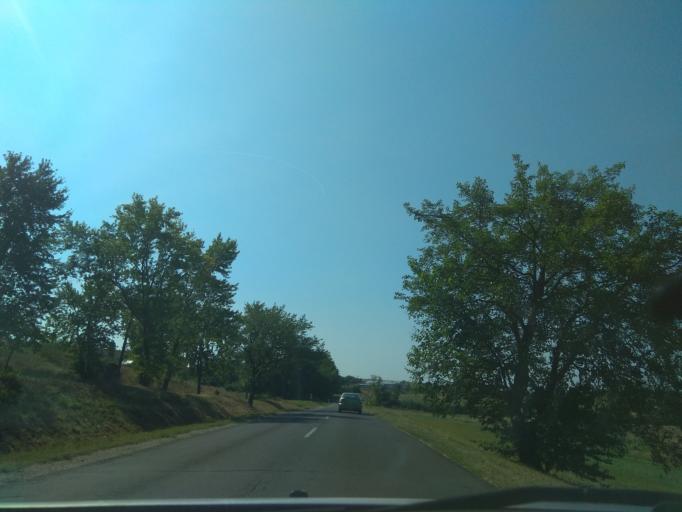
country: HU
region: Borsod-Abauj-Zemplen
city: Harsany
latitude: 47.9548
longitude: 20.7446
